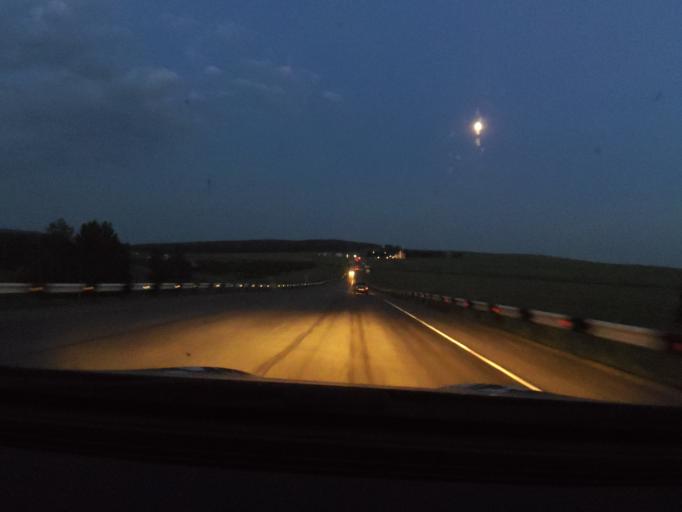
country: RU
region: Bashkortostan
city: Duvan
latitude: 55.9228
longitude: 58.2062
